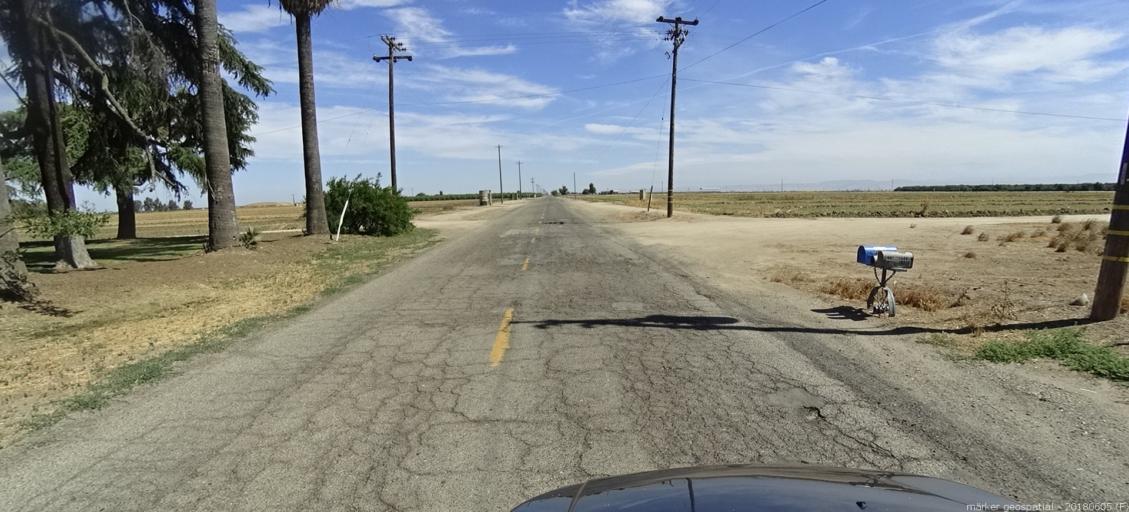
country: US
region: California
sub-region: Madera County
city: Chowchilla
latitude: 37.1159
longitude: -120.3827
